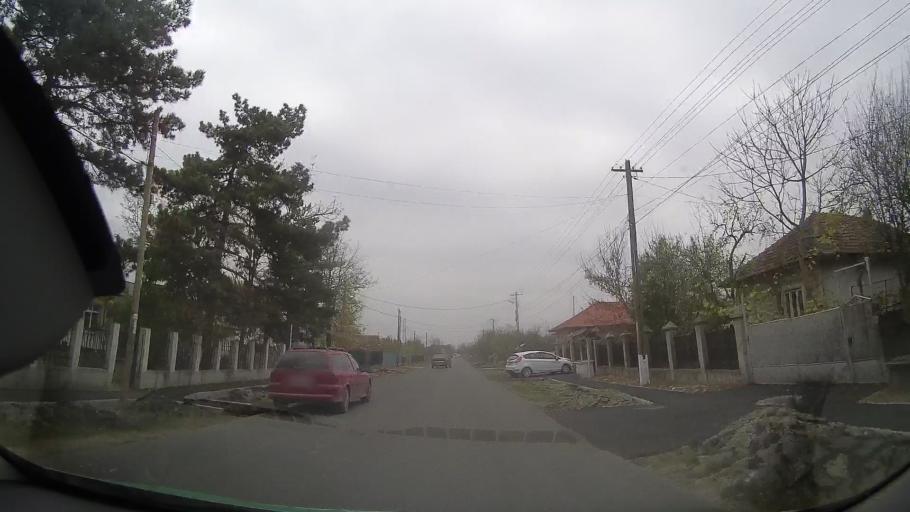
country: RO
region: Buzau
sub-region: Comuna Pogoanele
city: Pogoanele
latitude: 44.9228
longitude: 26.9940
